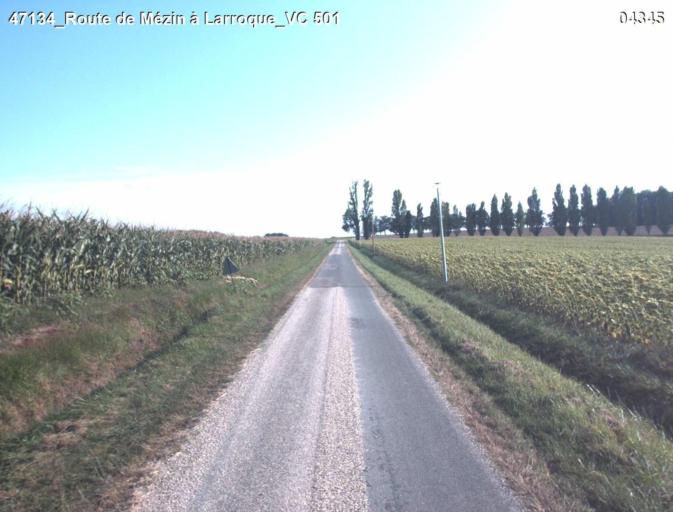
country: FR
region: Aquitaine
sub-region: Departement du Lot-et-Garonne
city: Mezin
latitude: 44.0334
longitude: 0.2675
